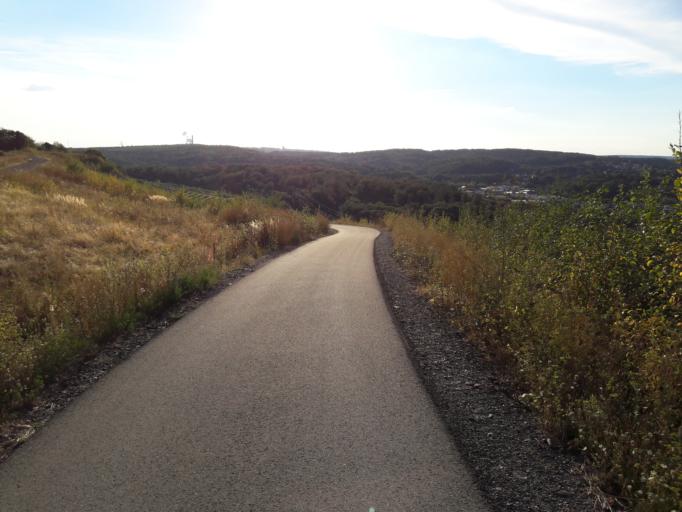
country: DE
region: Saarland
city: Schiffweiler
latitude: 49.3465
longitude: 7.1205
